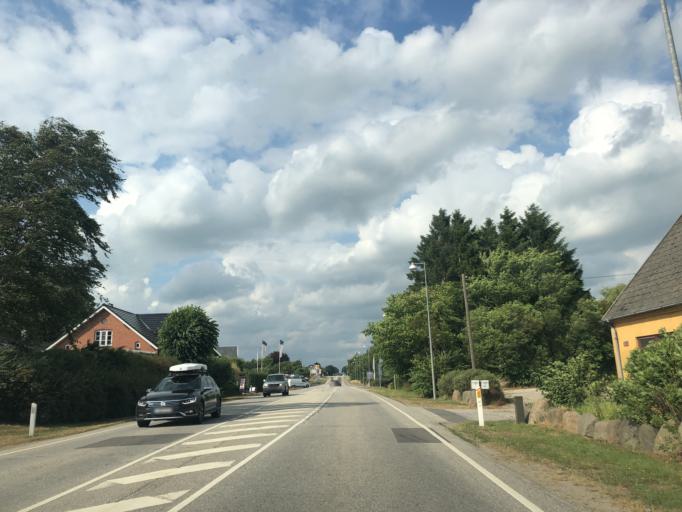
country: DK
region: Zealand
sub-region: Faxe Kommune
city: Ronnede
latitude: 55.3069
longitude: 12.0485
